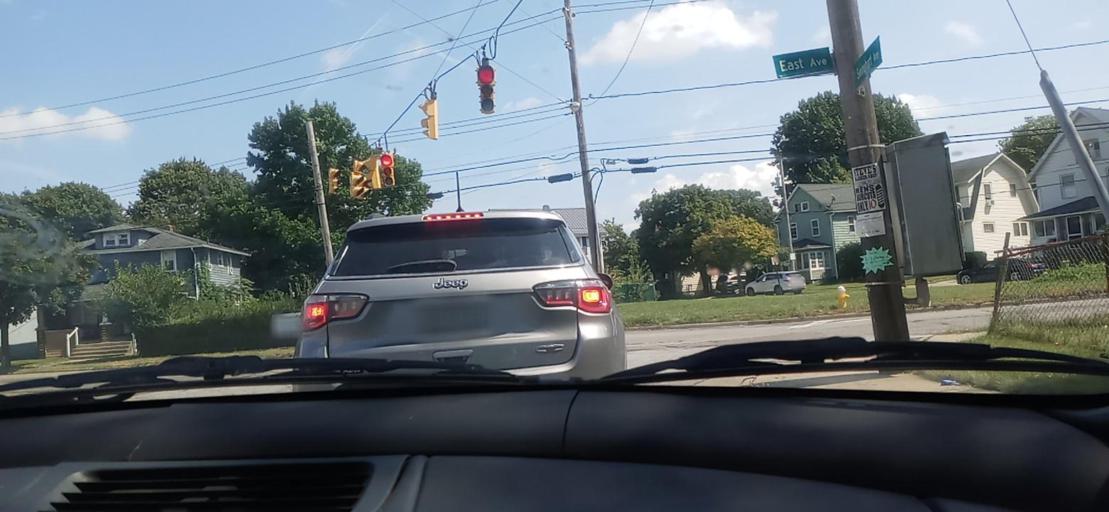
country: US
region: Ohio
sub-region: Summit County
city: Barberton
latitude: 41.0386
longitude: -81.5760
